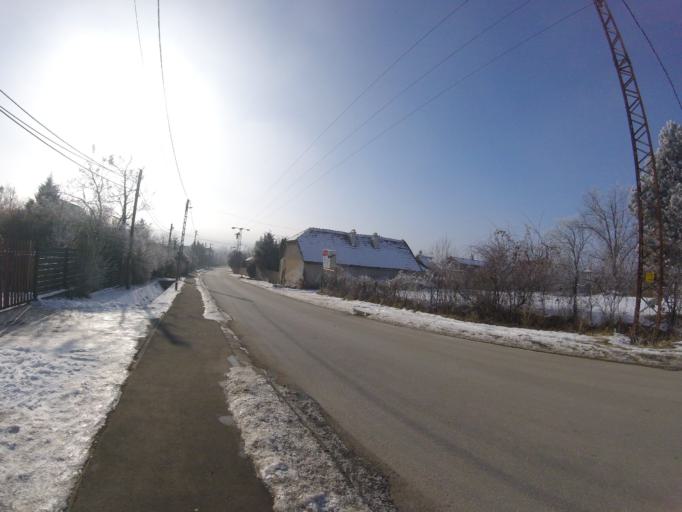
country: HU
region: Pest
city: Pilisszentivan
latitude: 47.5821
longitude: 18.8855
